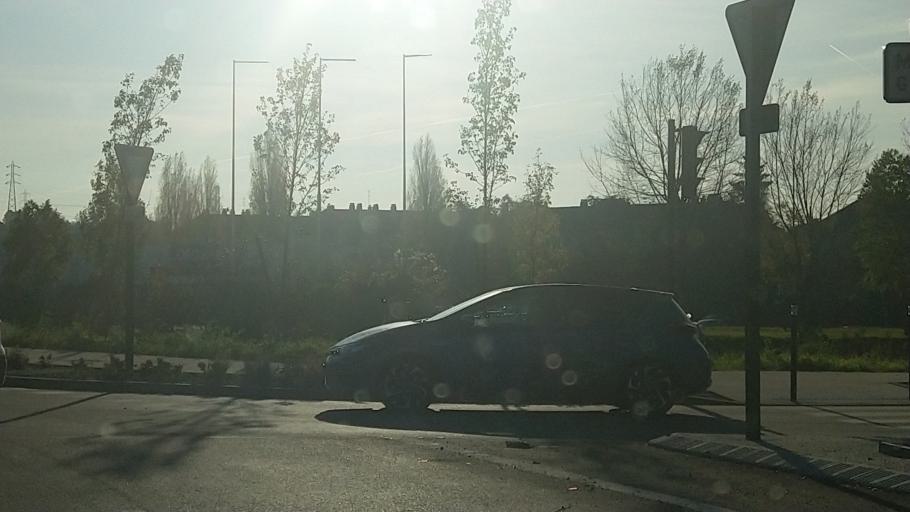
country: FR
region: Ile-de-France
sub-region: Departement du Val-d'Oise
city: Groslay
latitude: 48.9841
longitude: 2.3618
